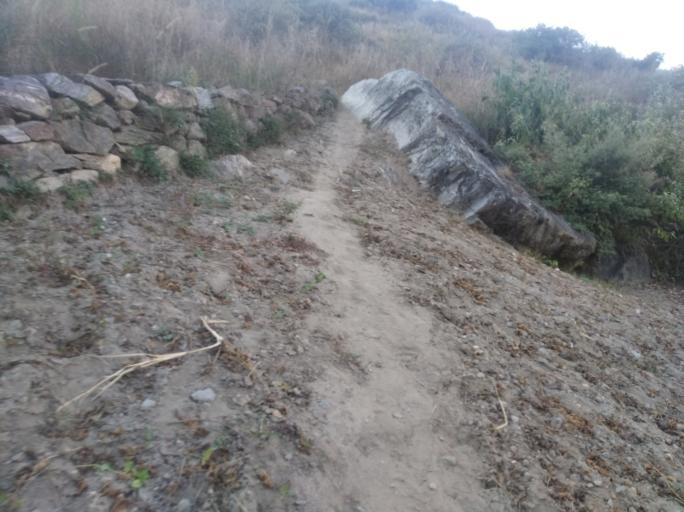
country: NP
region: Western Region
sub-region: Dhawalagiri Zone
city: Jomsom
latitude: 28.8728
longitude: 82.9980
